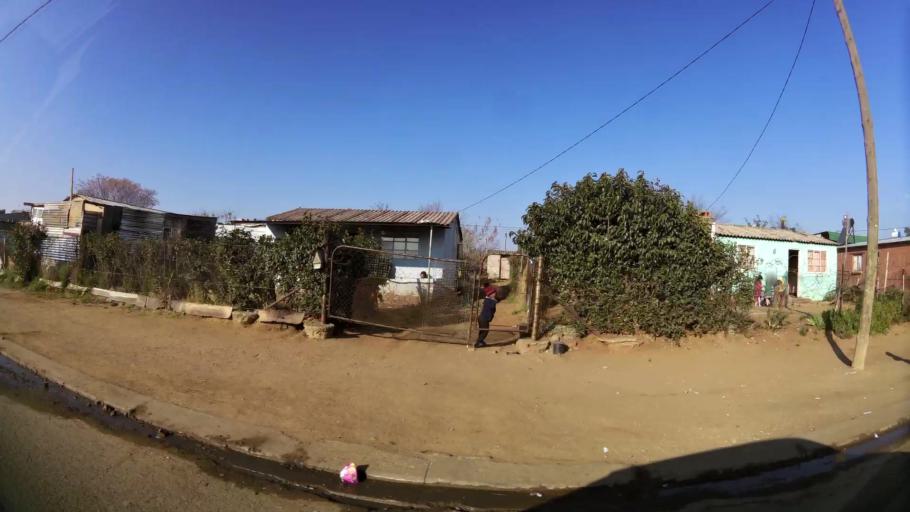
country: ZA
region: Orange Free State
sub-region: Mangaung Metropolitan Municipality
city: Bloemfontein
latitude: -29.1399
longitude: 26.2493
